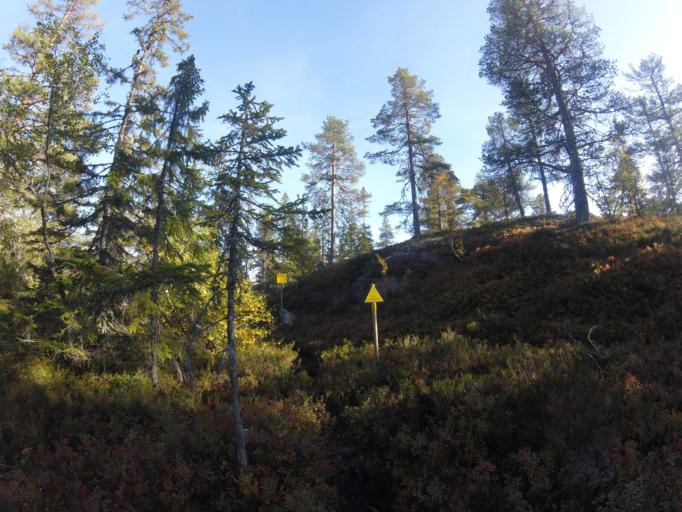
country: NO
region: Telemark
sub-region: Notodden
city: Notodden
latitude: 59.6806
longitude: 9.4000
